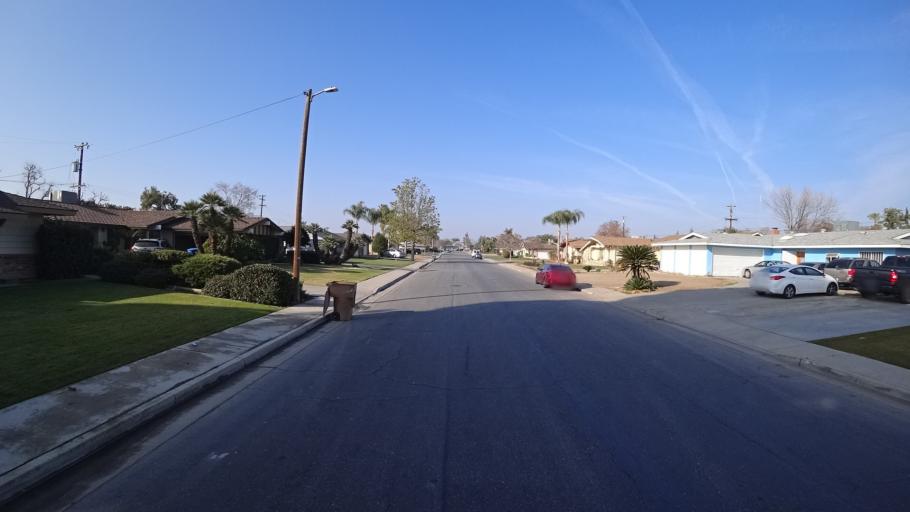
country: US
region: California
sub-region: Kern County
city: Bakersfield
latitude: 35.3282
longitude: -119.0288
